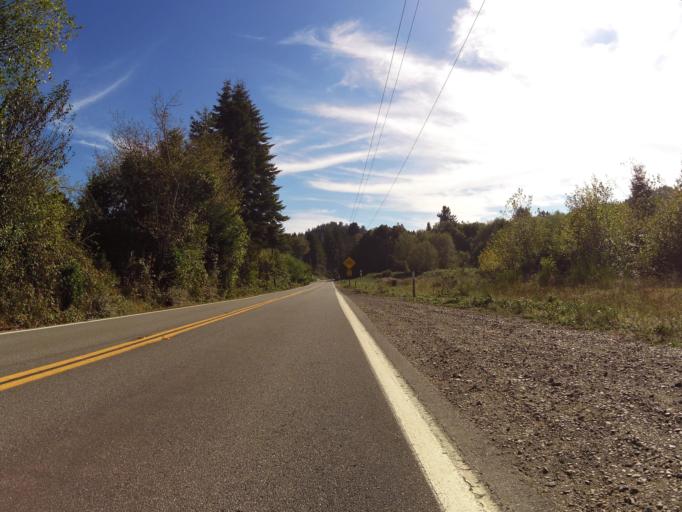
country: US
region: California
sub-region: Del Norte County
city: Bertsch-Oceanview
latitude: 41.8611
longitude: -124.1178
